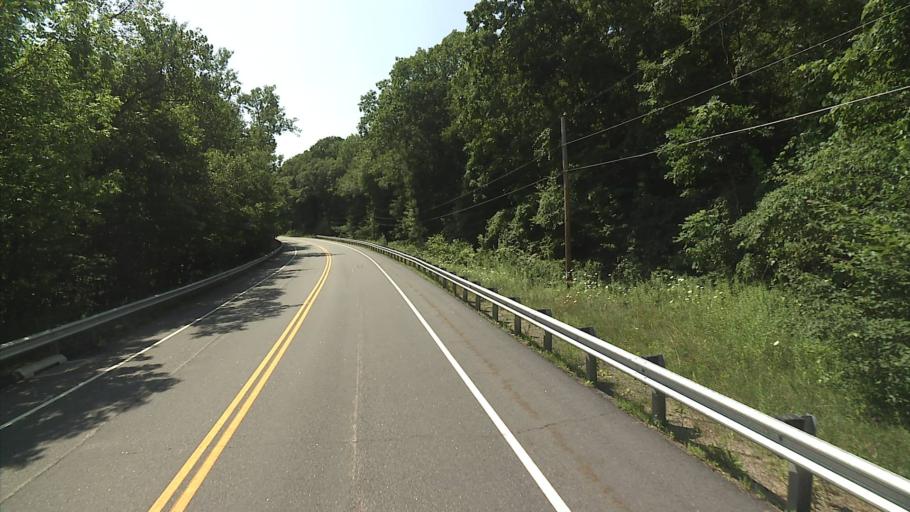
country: US
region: Connecticut
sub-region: Litchfield County
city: Winchester Center
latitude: 41.8906
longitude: -73.1764
